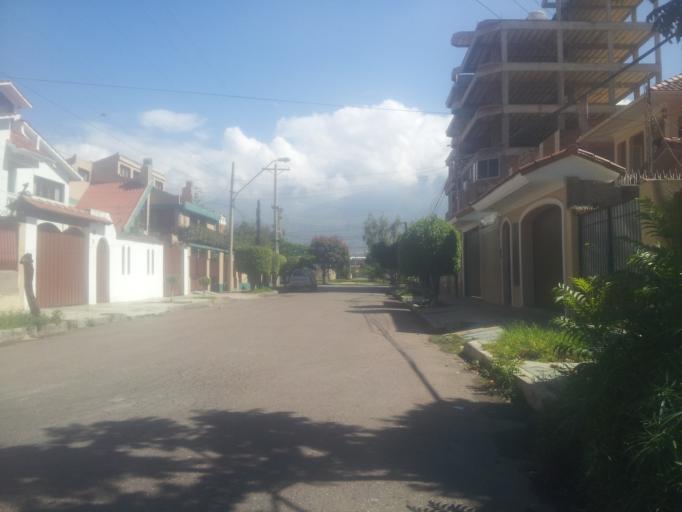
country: BO
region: Cochabamba
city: Cochabamba
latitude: -17.3805
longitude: -66.1729
